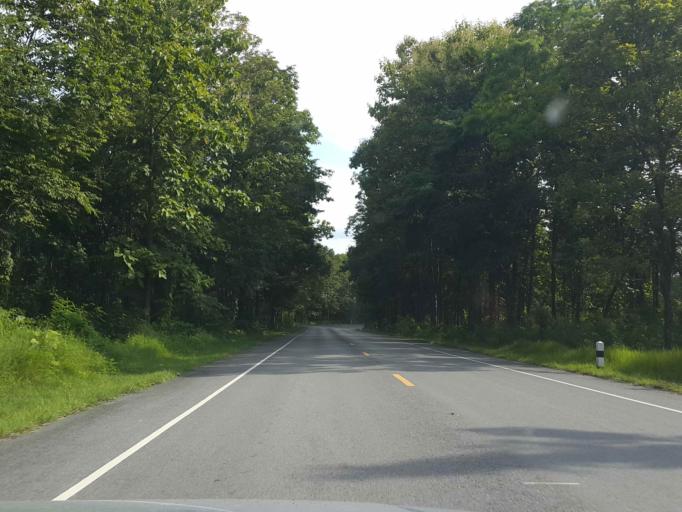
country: TH
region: Uttaradit
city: Lap Lae
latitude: 17.8153
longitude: 99.8606
